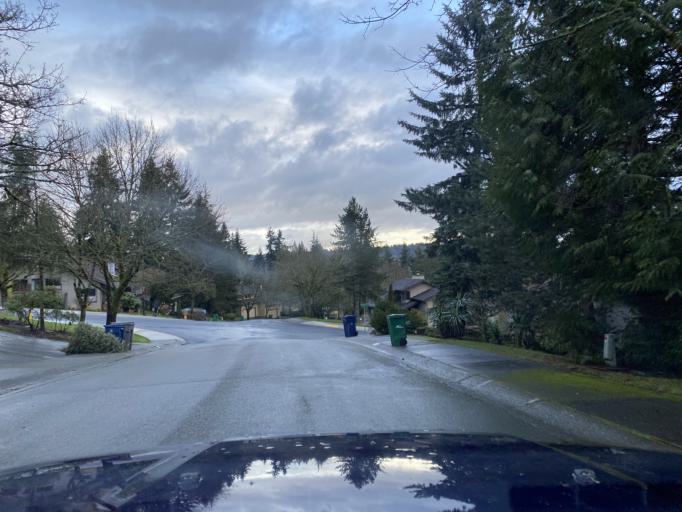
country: US
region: Washington
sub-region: King County
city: Redmond
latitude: 47.6636
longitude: -122.1305
